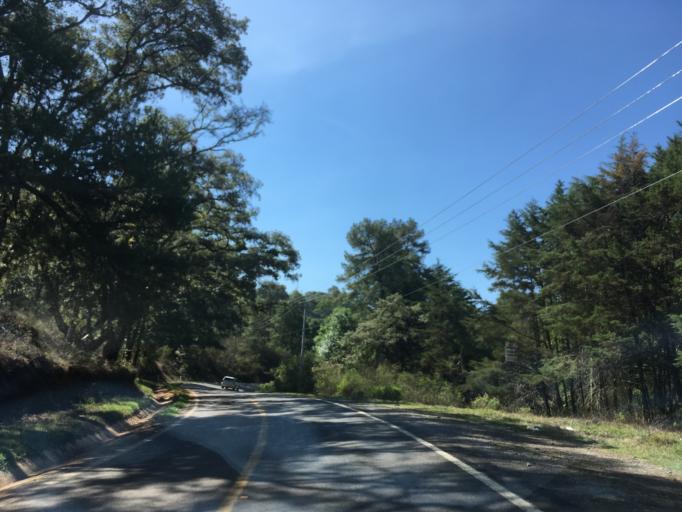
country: MX
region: Michoacan
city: Charo
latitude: 19.6643
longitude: -101.0040
